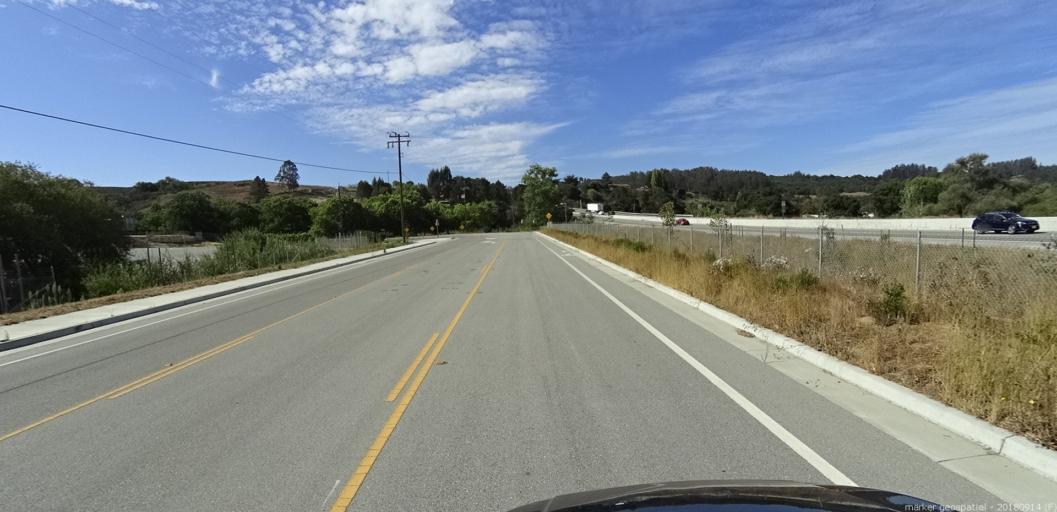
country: US
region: California
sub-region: San Benito County
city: Aromas
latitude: 36.8538
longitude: -121.6335
